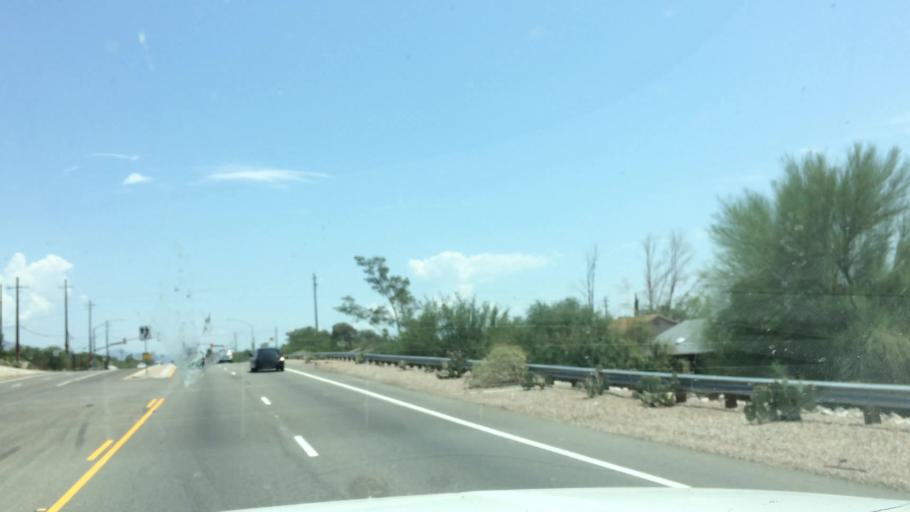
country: US
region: Arizona
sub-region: Pima County
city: Flowing Wells
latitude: 32.3231
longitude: -111.0314
